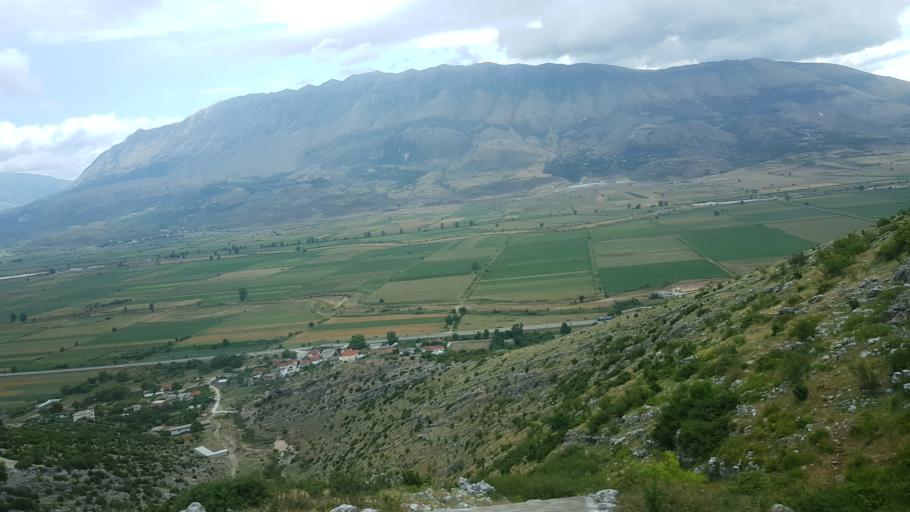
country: AL
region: Gjirokaster
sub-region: Rrethi i Gjirokastres
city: Libohove
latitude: 39.9482
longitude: 20.2448
